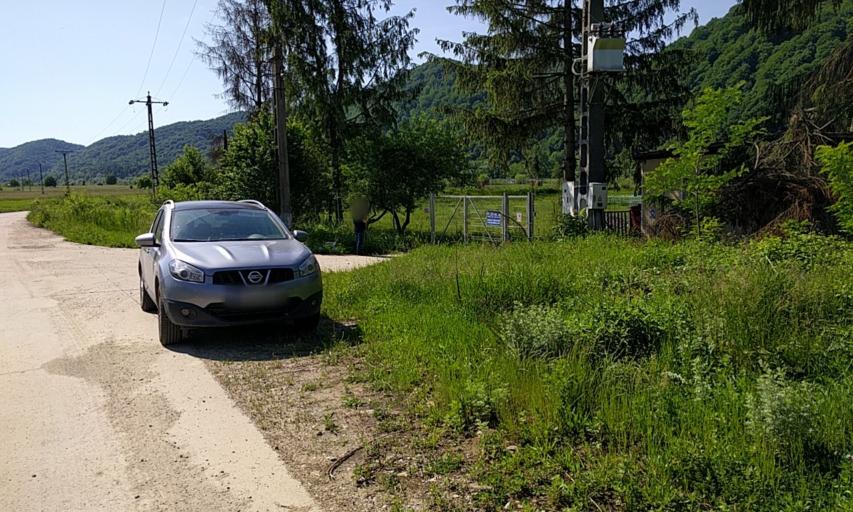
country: RO
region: Bistrita-Nasaud
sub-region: Oras Nasaud
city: Nasaud
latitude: 47.2946
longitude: 24.3784
